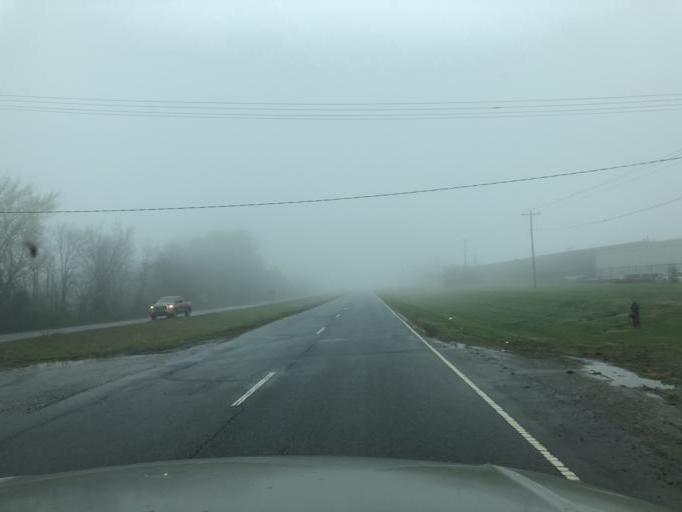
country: US
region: North Carolina
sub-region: Cleveland County
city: White Plains
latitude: 35.1865
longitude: -81.4113
